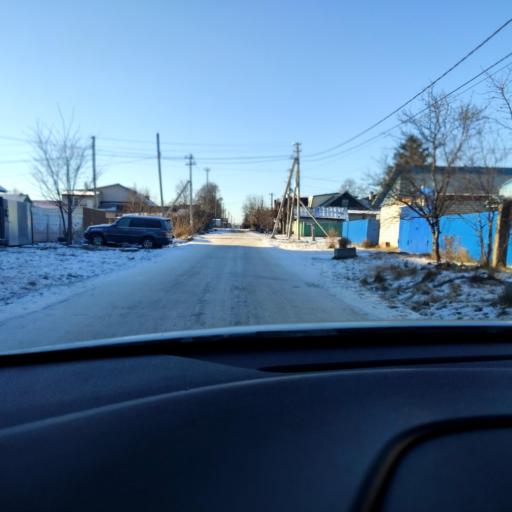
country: RU
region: Tatarstan
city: Staroye Arakchino
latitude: 55.8804
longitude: 49.0526
